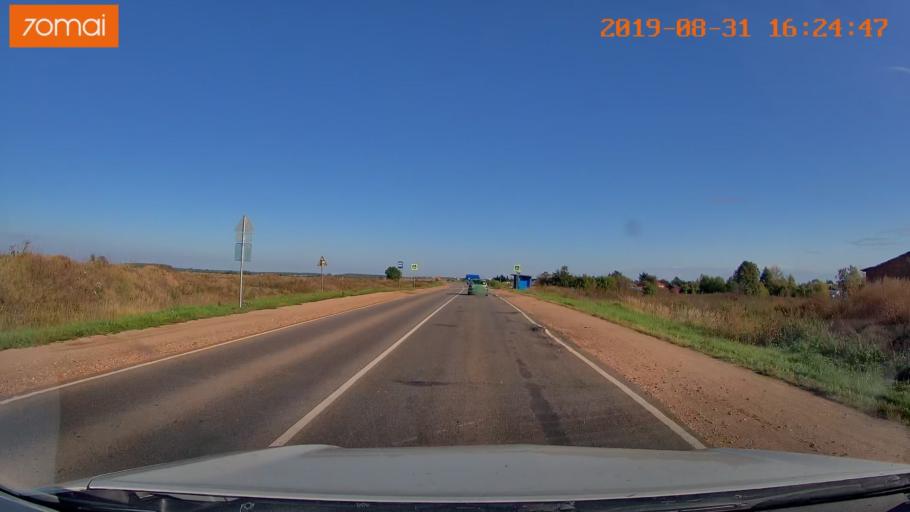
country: RU
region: Kaluga
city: Babynino
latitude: 54.5208
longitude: 35.7005
